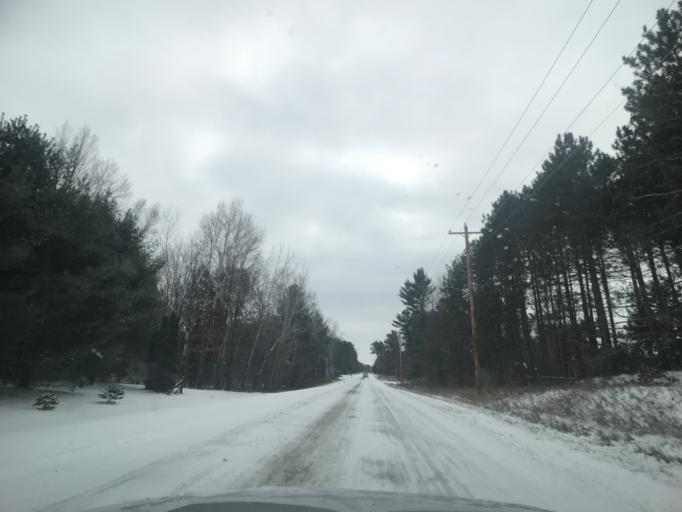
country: US
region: Wisconsin
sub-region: Brown County
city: Suamico
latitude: 44.7009
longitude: -88.1010
